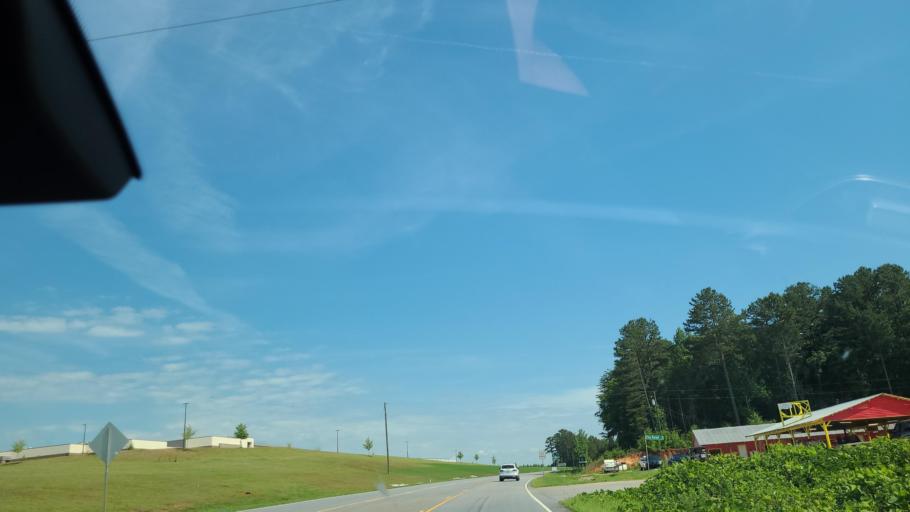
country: US
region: South Carolina
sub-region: Oconee County
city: Westminster
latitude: 34.6972
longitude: -83.0498
